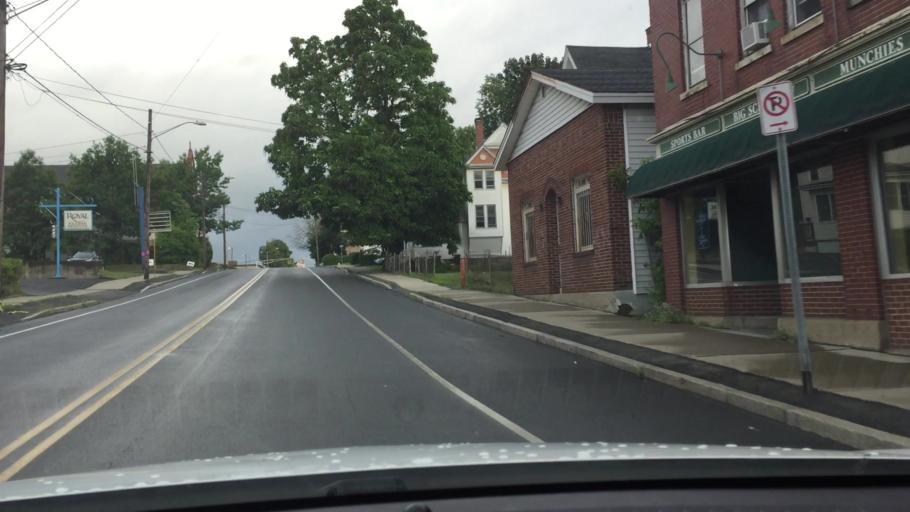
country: US
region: Massachusetts
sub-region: Berkshire County
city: Pittsfield
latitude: 42.4490
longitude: -73.2450
